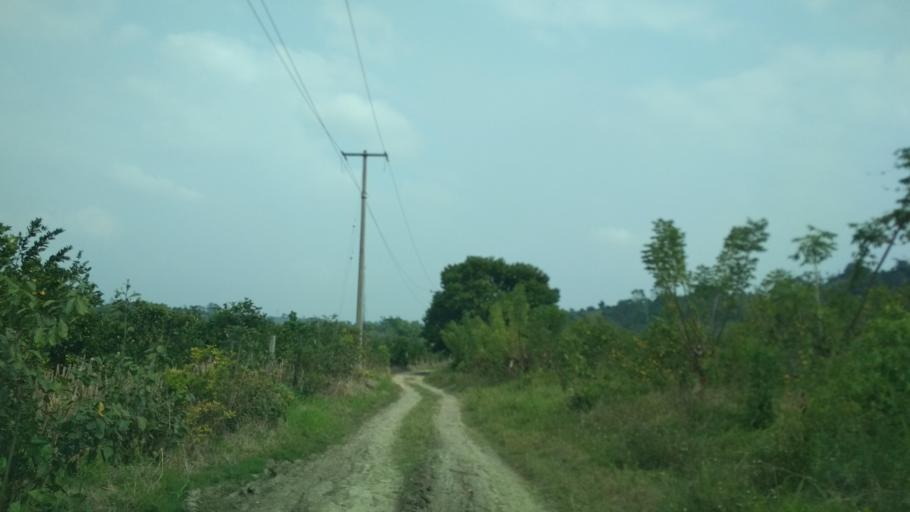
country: MM
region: Kayah
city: Loikaw
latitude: 20.2063
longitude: 97.3172
